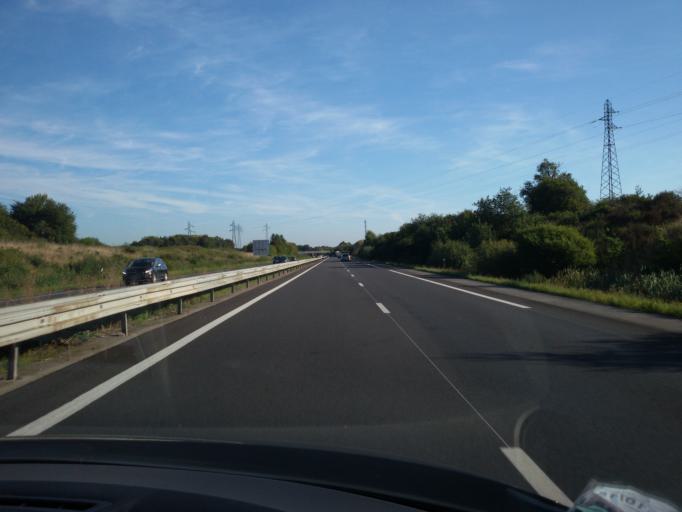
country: FR
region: Centre
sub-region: Departement du Loir-et-Cher
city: Theillay
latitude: 47.3069
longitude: 2.0477
